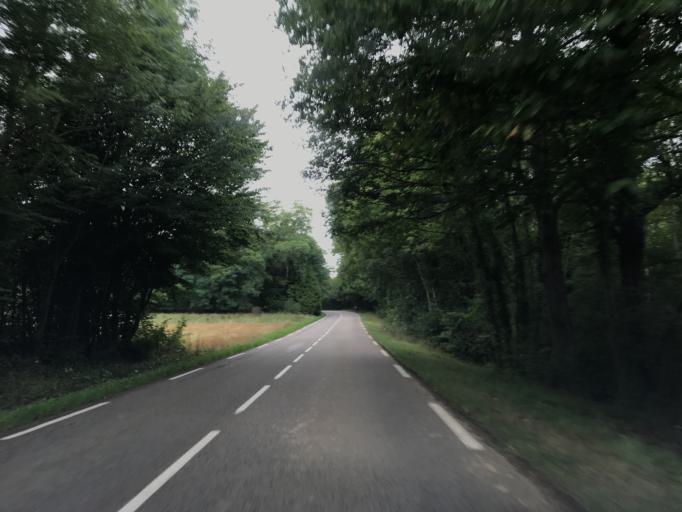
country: FR
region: Haute-Normandie
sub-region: Departement de l'Eure
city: Gravigny
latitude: 49.0321
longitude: 1.2663
